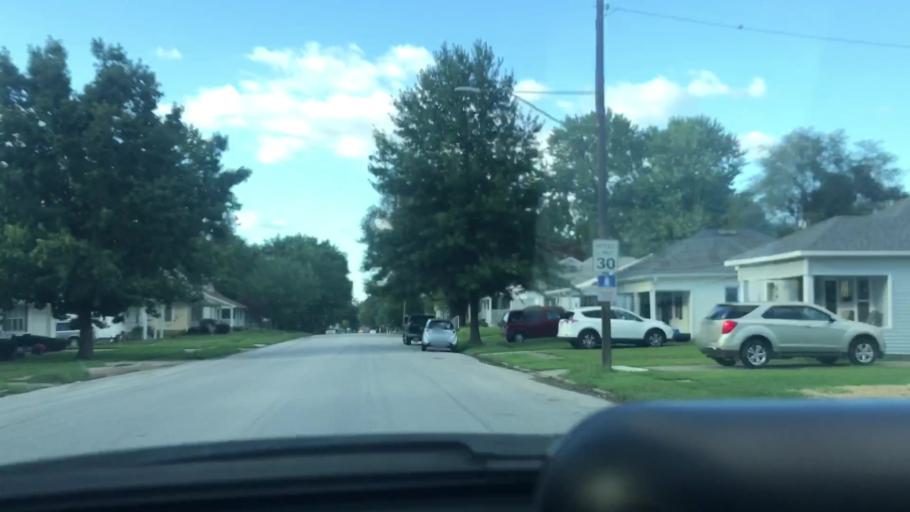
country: US
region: Missouri
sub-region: Pettis County
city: Sedalia
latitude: 38.6949
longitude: -93.2369
